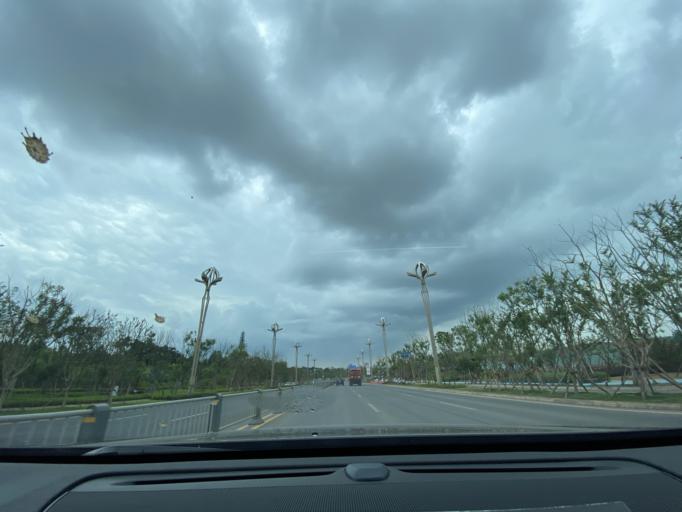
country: CN
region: Sichuan
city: Jiancheng
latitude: 30.4989
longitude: 104.4670
